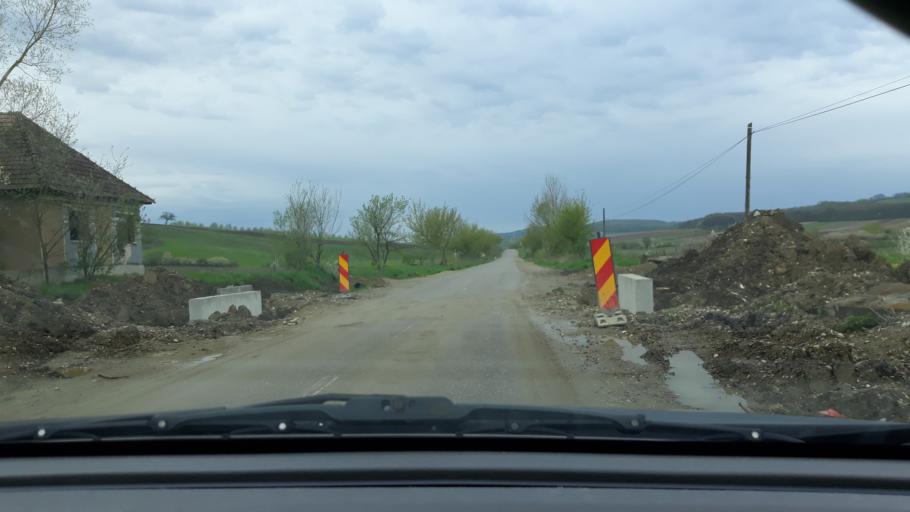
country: RO
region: Salaj
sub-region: Comuna Salatig
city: Salatig
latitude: 47.3826
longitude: 23.1472
